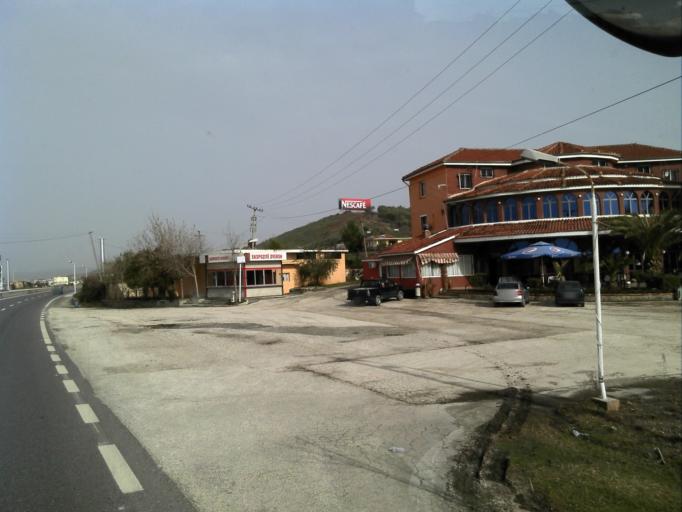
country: AL
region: Fier
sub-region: Rrethi i Lushnjes
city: Golem
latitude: 41.0069
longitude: 19.6637
